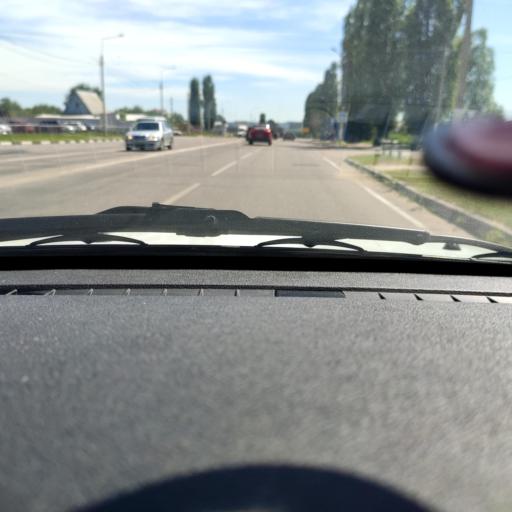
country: RU
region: Voronezj
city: Semiluki
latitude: 51.7267
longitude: 39.0430
